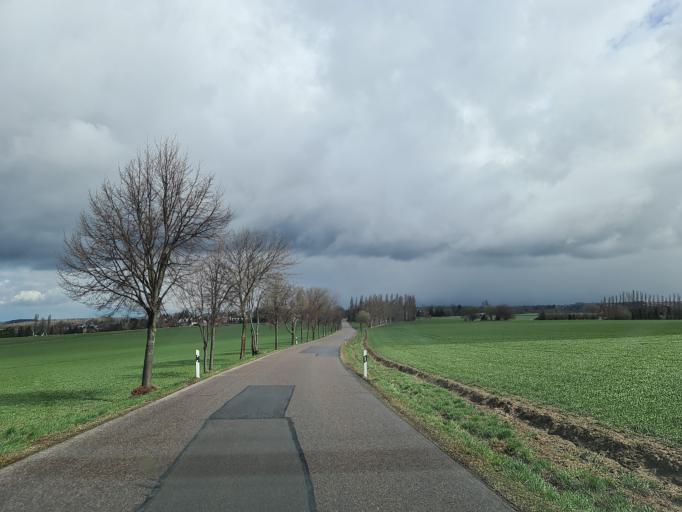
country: DE
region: Saxony
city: Limbach-Oberfrohna
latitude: 50.8398
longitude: 12.7289
